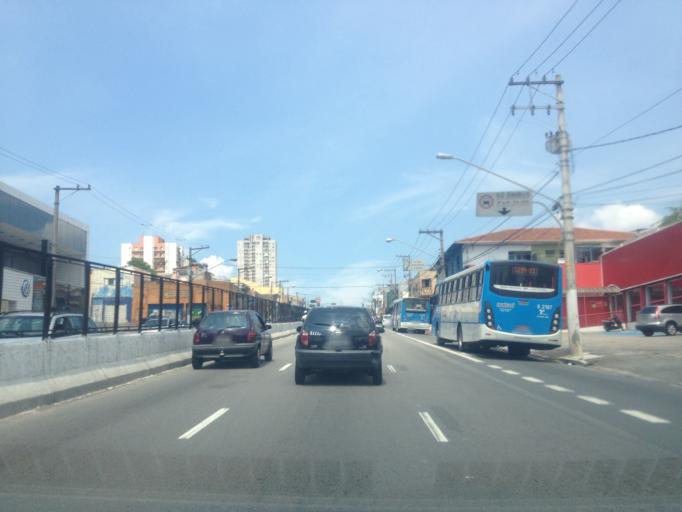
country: BR
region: Sao Paulo
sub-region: Diadema
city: Diadema
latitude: -23.6360
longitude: -46.6700
